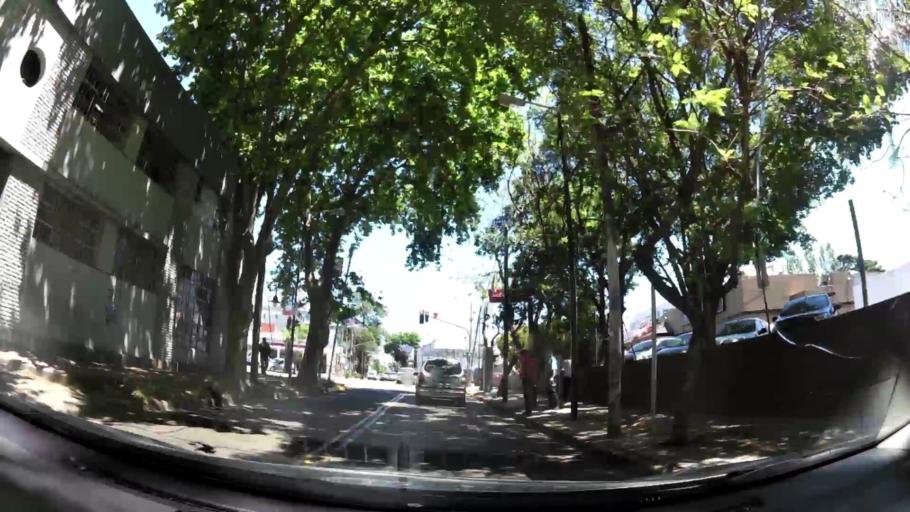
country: AR
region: Buenos Aires
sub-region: Partido de Tigre
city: Tigre
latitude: -34.4462
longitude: -58.5459
